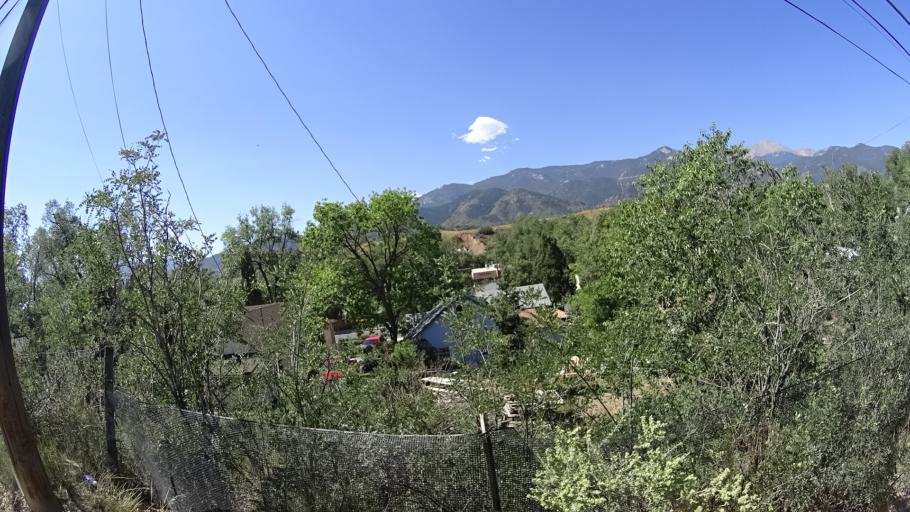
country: US
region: Colorado
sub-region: El Paso County
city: Manitou Springs
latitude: 38.8550
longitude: -104.8724
